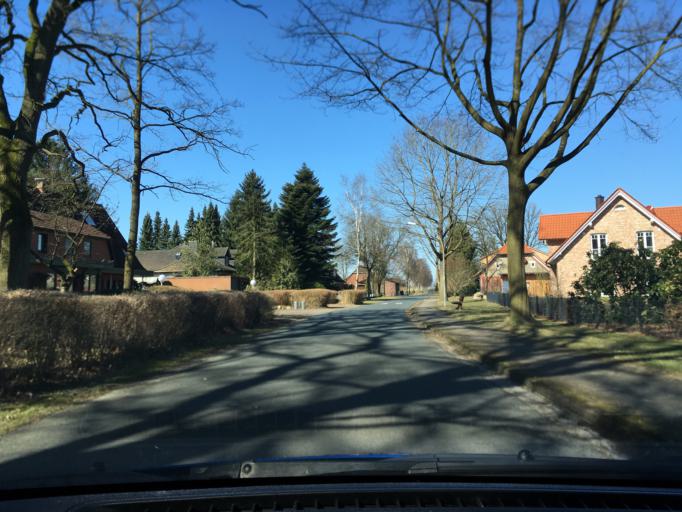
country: DE
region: Lower Saxony
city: Hemslingen
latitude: 53.0836
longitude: 9.5980
